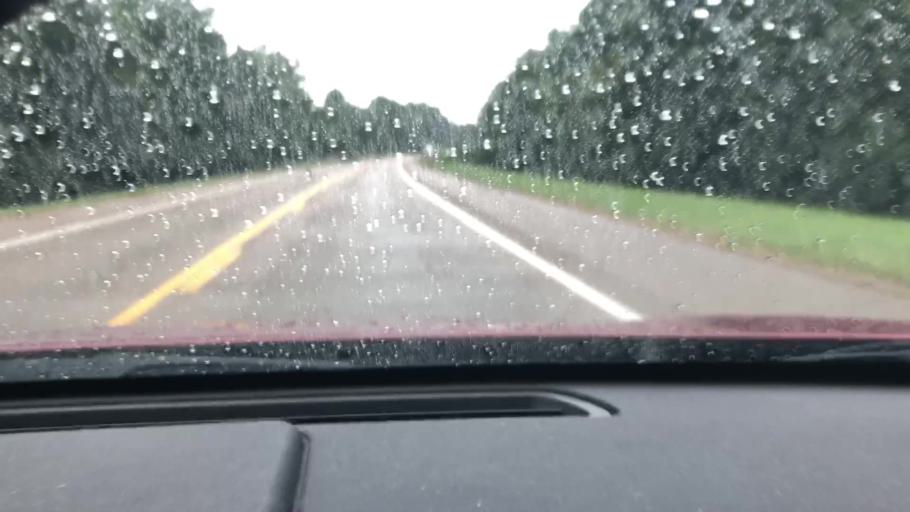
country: US
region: Arkansas
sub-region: Columbia County
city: Magnolia
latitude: 33.2966
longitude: -93.2564
